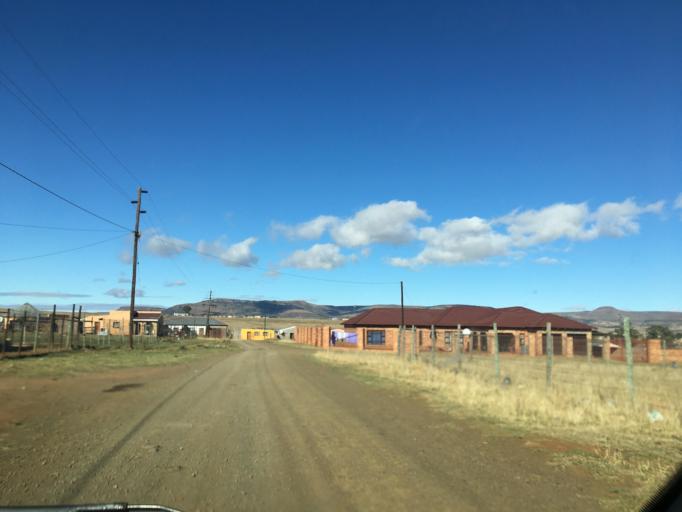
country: ZA
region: Eastern Cape
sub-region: Chris Hani District Municipality
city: Cala
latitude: -31.5387
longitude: 27.6941
